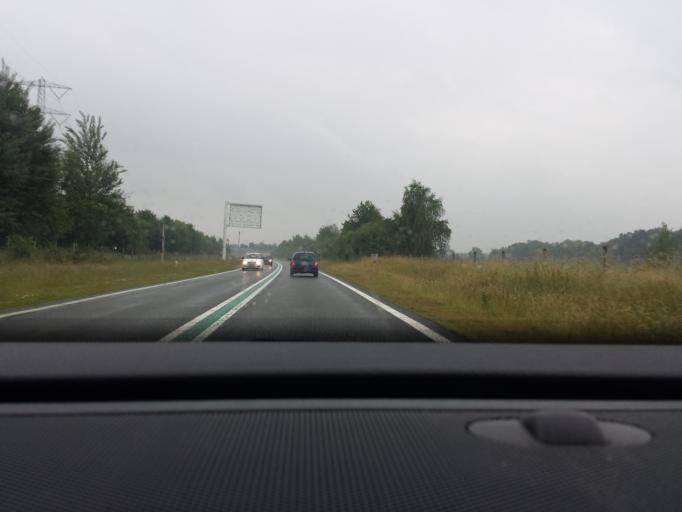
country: NL
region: Overijssel
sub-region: Gemeente Enschede
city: Enschede
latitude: 52.1976
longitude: 6.9405
